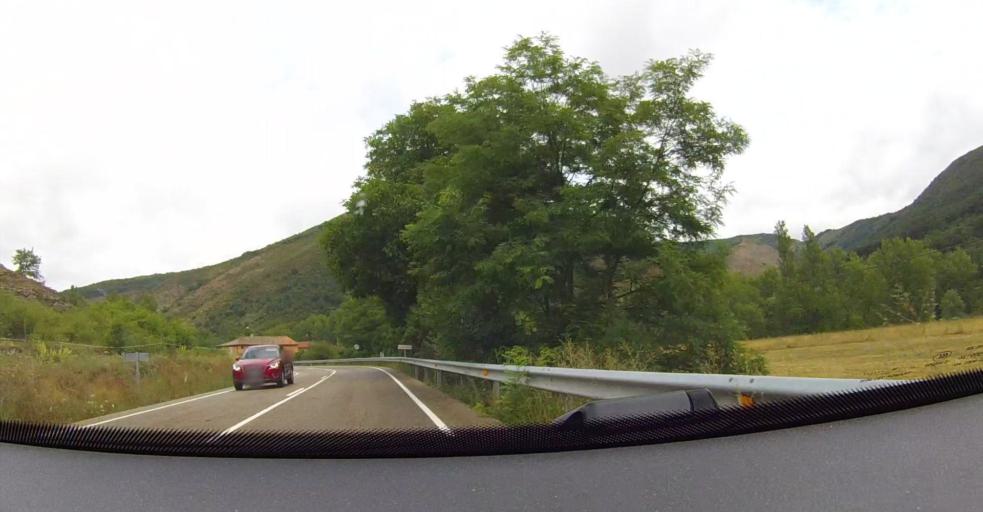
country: ES
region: Castille and Leon
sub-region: Provincia de Leon
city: Bonar
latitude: 42.8859
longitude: -5.3092
